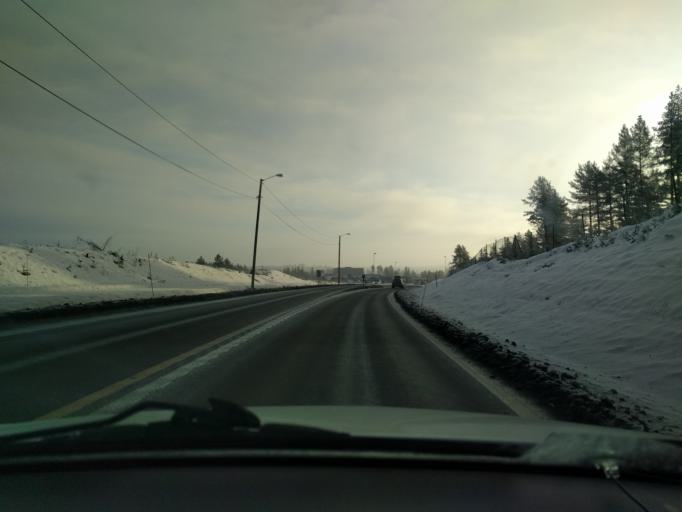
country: NO
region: Hedmark
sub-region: Elverum
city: Elverum
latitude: 60.8844
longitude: 11.5263
